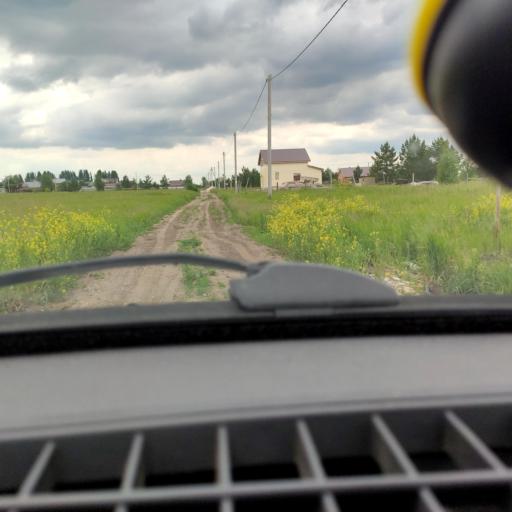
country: RU
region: Samara
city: Povolzhskiy
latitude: 53.5978
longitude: 49.5824
